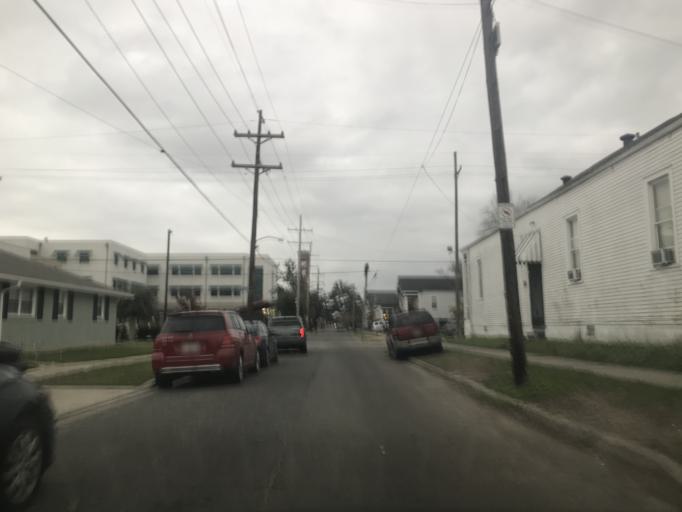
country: US
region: Louisiana
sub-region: Orleans Parish
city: New Orleans
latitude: 29.9666
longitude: -90.0938
